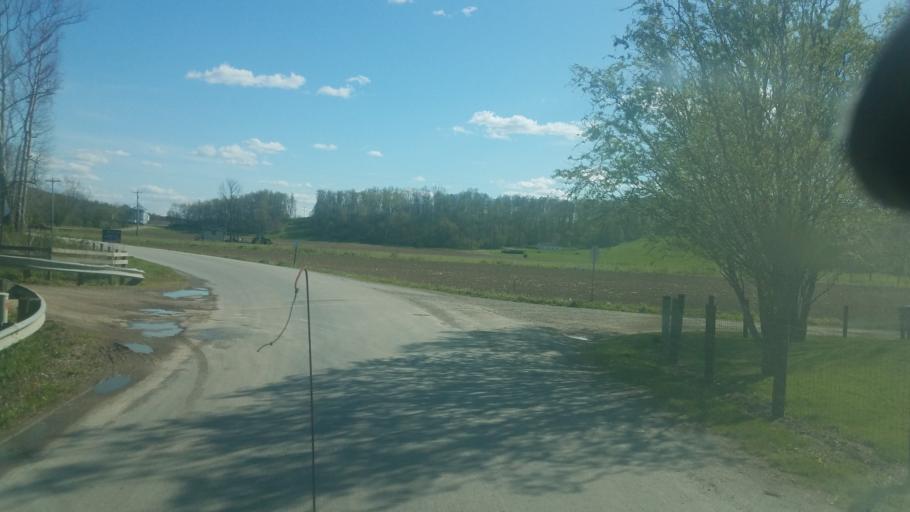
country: US
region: Ohio
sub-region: Coshocton County
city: Coshocton
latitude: 40.3947
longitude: -81.8459
